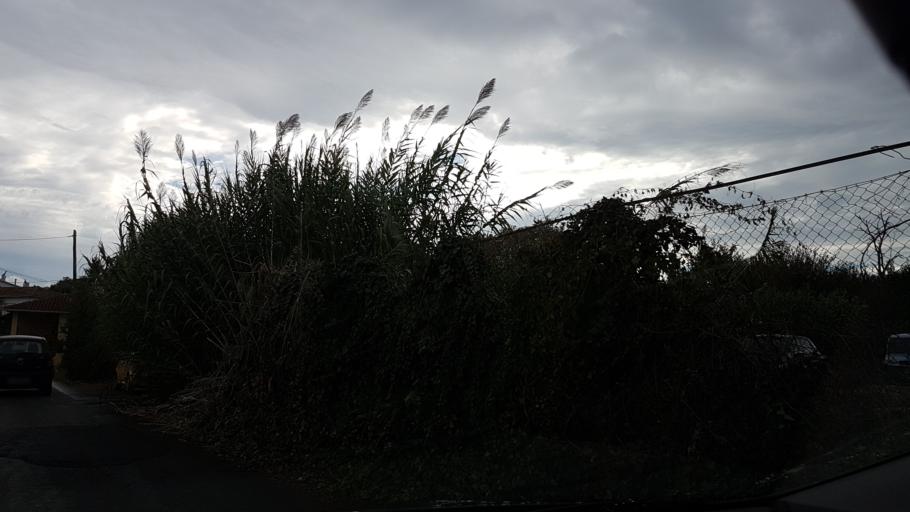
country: GR
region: Ionian Islands
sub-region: Nomos Kerkyras
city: Kerkyra
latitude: 39.6178
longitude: 19.9079
